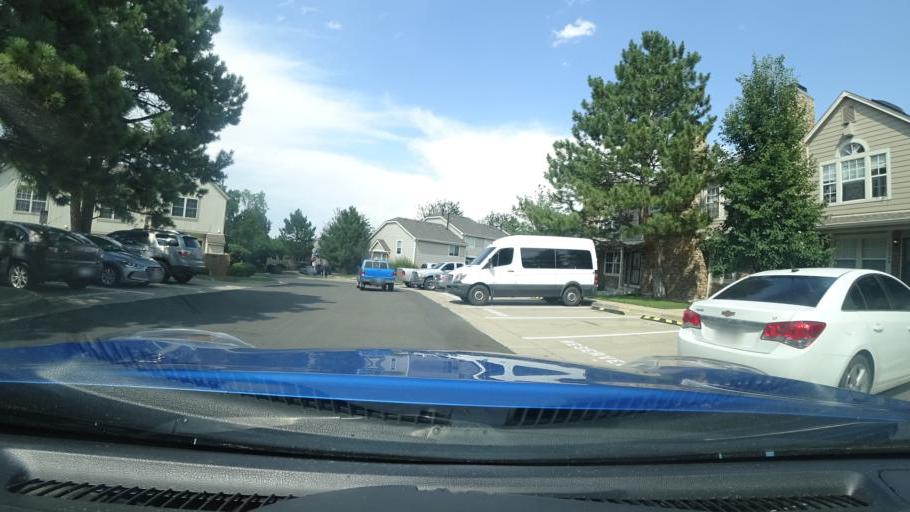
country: US
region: Colorado
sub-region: Adams County
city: Aurora
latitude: 39.6942
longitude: -104.7753
